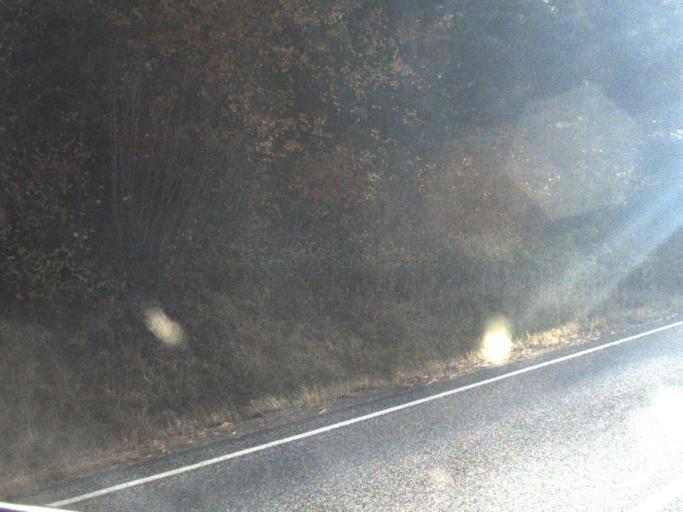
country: CA
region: British Columbia
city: Rossland
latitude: 48.8720
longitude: -117.8577
